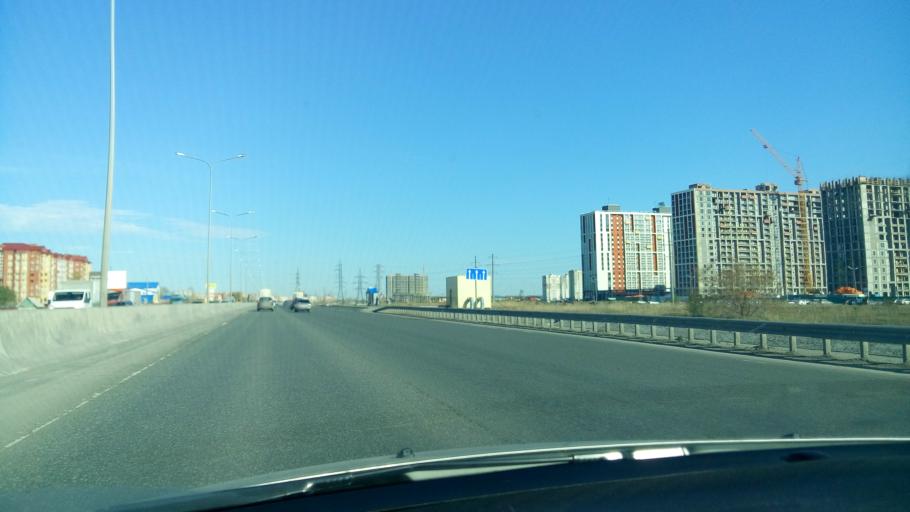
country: RU
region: Tjumen
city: Tyumen
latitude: 57.1283
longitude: 65.4872
